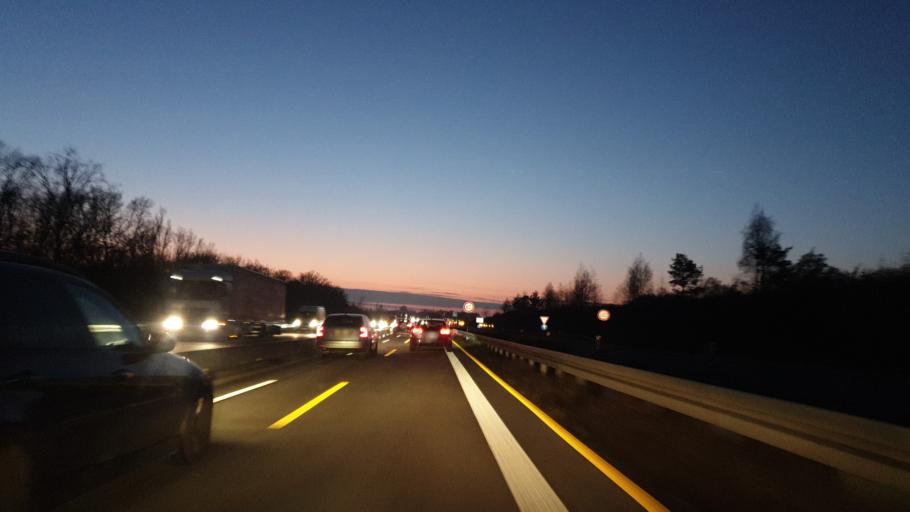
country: DE
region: Saxony
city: Reinsberg
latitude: 51.0607
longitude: 13.4062
